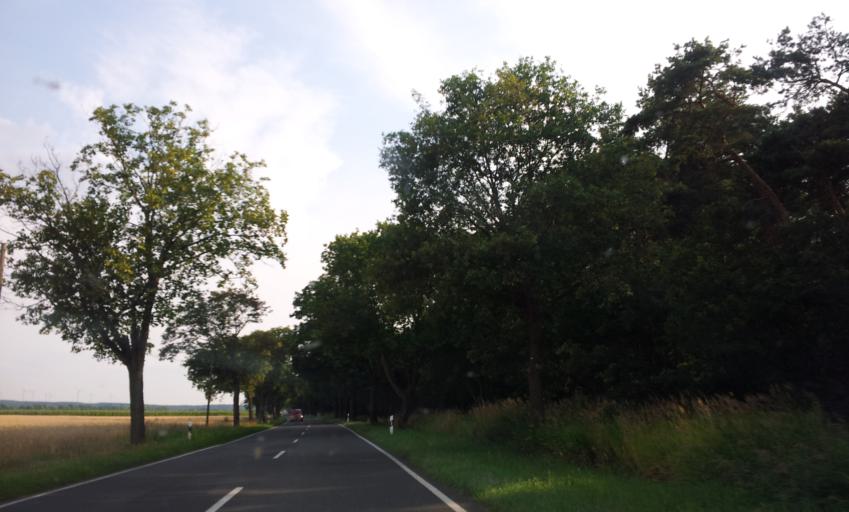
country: DE
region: Brandenburg
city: Treuenbrietzen
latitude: 52.0976
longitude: 12.9478
